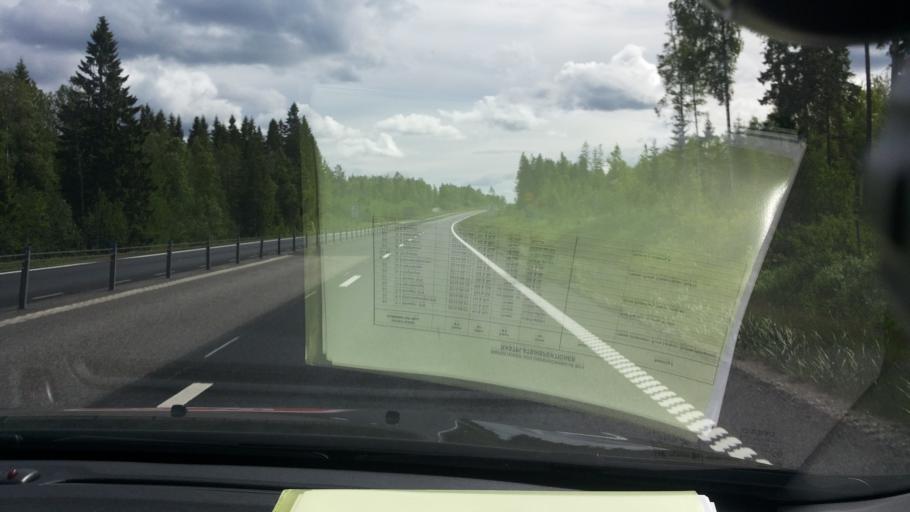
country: SE
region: Vaesternorrland
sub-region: Sundsvalls Kommun
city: Njurundabommen
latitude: 62.2132
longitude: 17.3734
